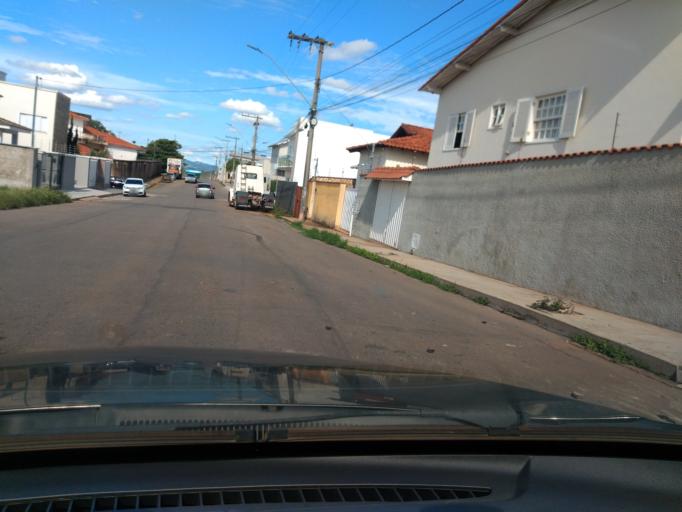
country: BR
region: Minas Gerais
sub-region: Tres Coracoes
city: Tres Coracoes
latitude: -21.6880
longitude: -45.2642
